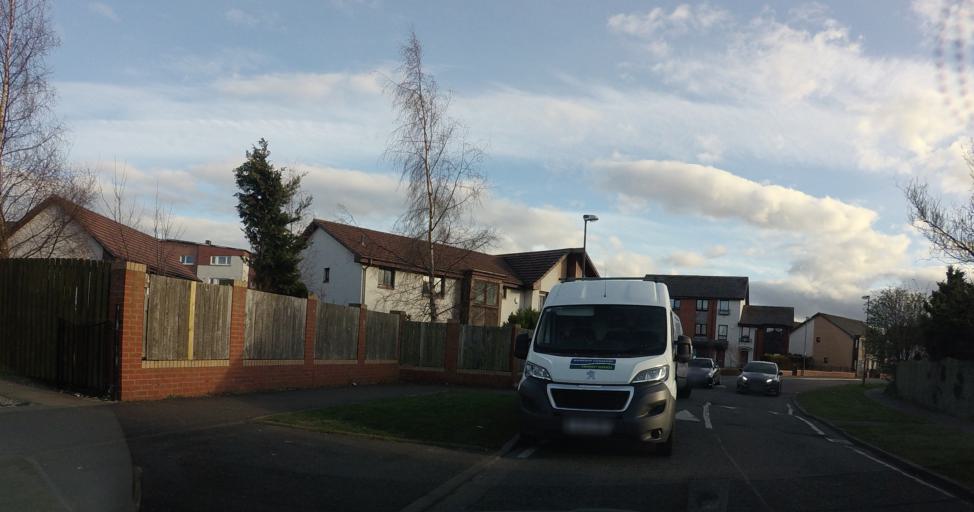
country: GB
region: Scotland
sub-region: Midlothian
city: Loanhead
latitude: 55.9002
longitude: -3.1562
